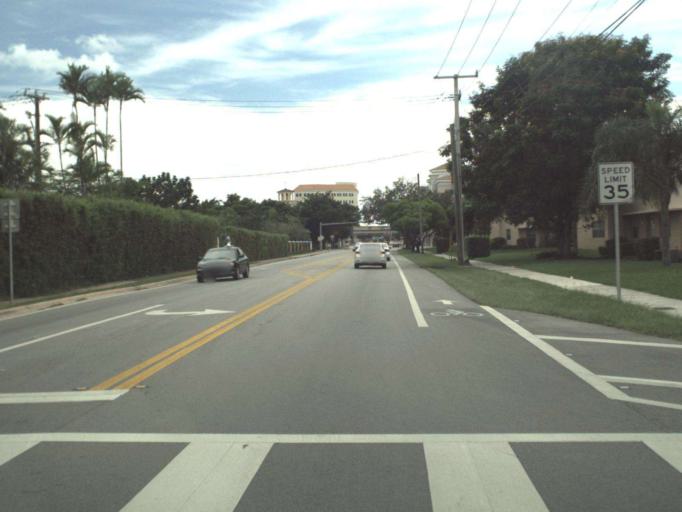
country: US
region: Florida
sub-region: Miami-Dade County
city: South Miami
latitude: 25.7116
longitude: -80.2857
